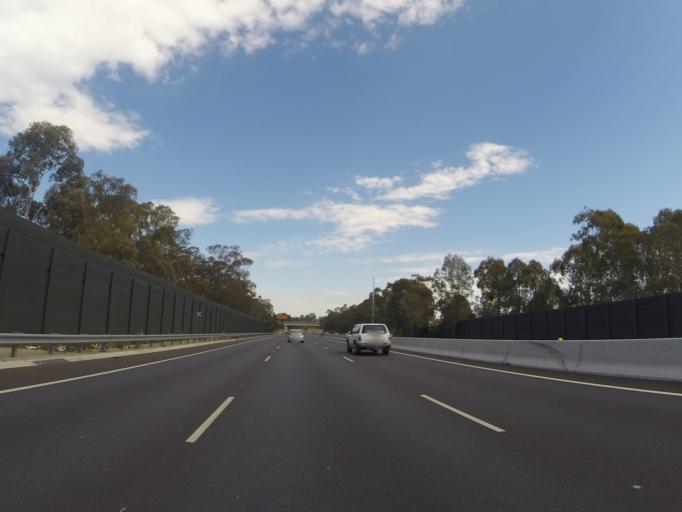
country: AU
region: New South Wales
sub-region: Campbelltown Municipality
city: Glenfield
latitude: -33.9436
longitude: 150.8992
